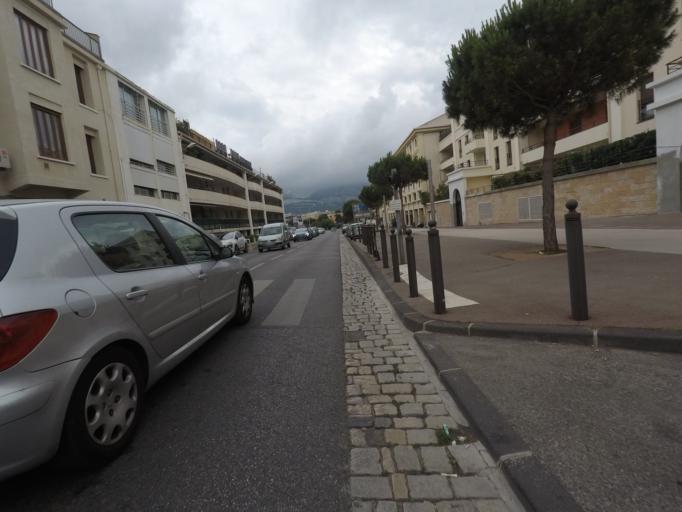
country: FR
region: Provence-Alpes-Cote d'Azur
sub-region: Departement des Bouches-du-Rhone
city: Marseille 08
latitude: 43.2558
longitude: 5.3823
